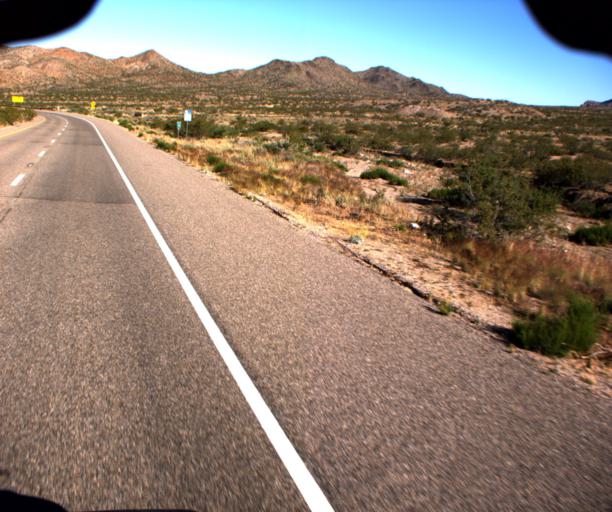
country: US
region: Nevada
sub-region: Clark County
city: Laughlin
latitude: 35.1990
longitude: -114.4197
